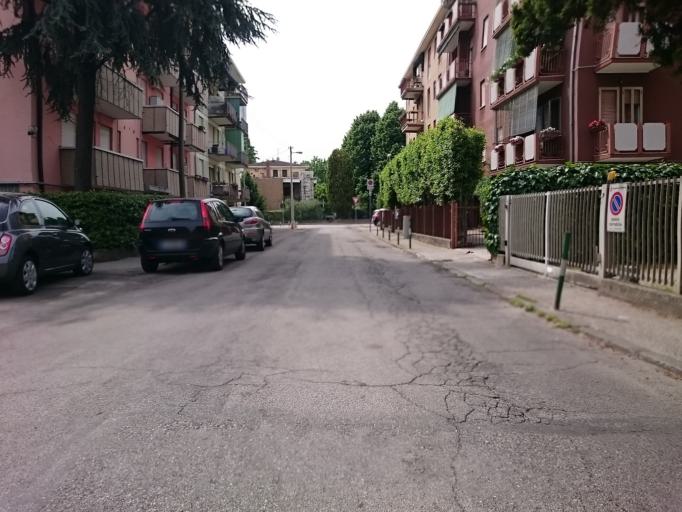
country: IT
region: Veneto
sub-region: Provincia di Padova
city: Padova
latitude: 45.3877
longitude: 11.8775
